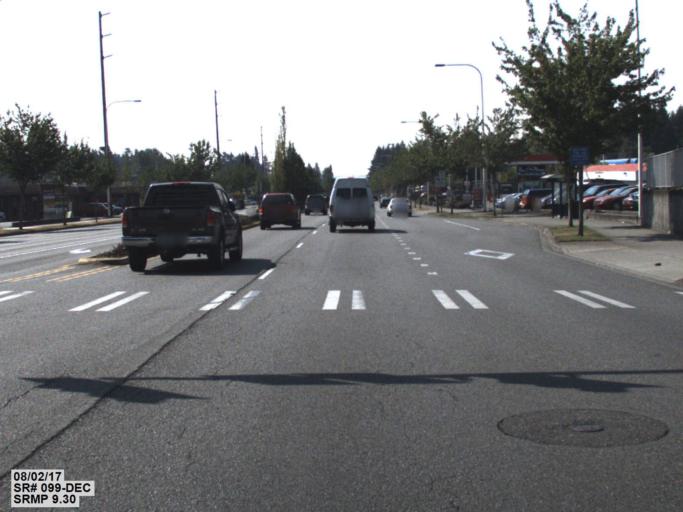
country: US
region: Washington
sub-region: King County
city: Federal Way
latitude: 47.3059
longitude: -122.3135
